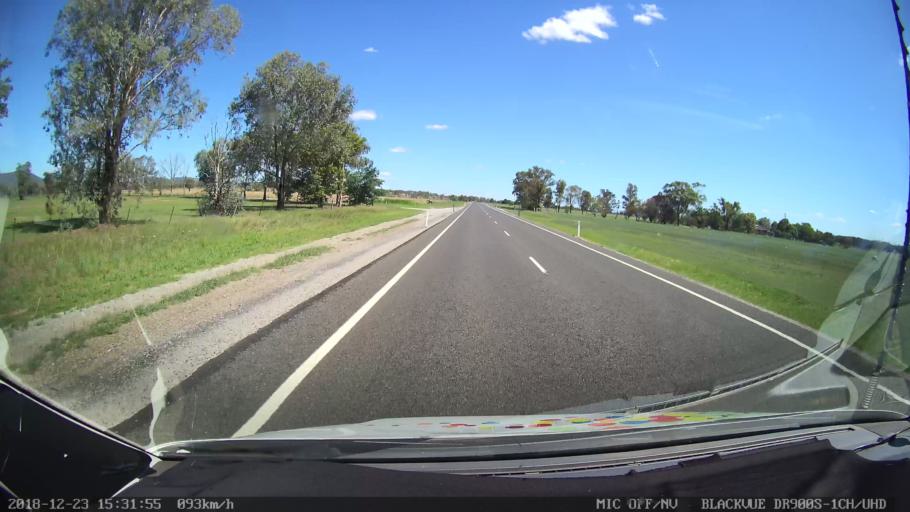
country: AU
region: New South Wales
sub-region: Tamworth Municipality
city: East Tamworth
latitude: -30.9784
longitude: 150.8691
